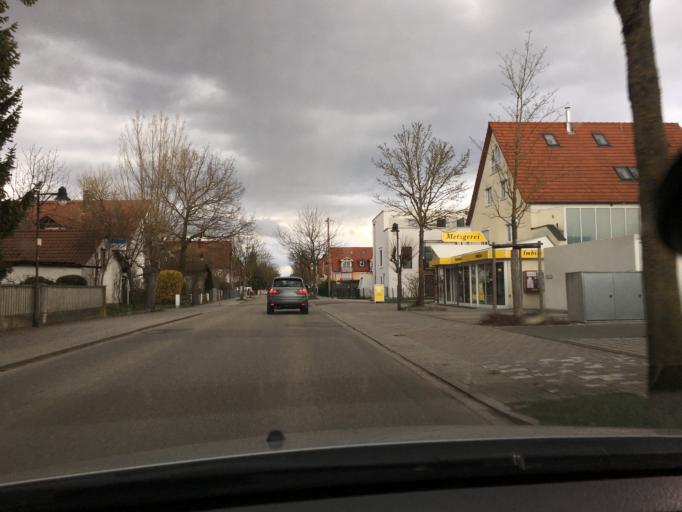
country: DE
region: Bavaria
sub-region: Upper Bavaria
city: Hallbergmoos
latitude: 48.3250
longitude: 11.7503
